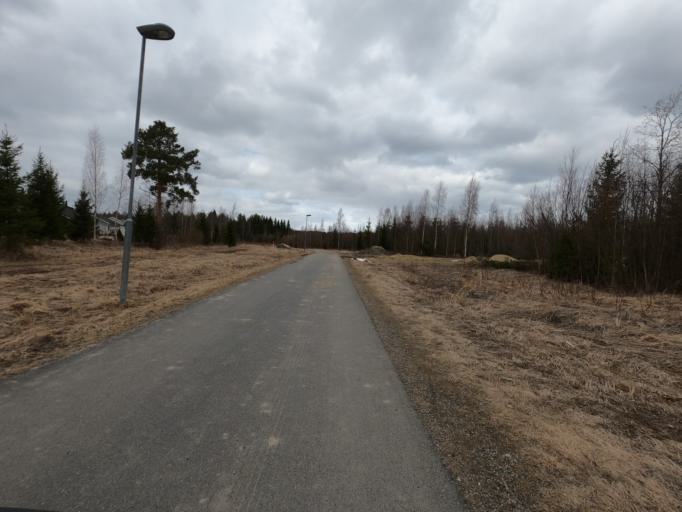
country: FI
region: North Karelia
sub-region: Joensuu
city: Joensuu
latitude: 62.5673
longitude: 29.8171
